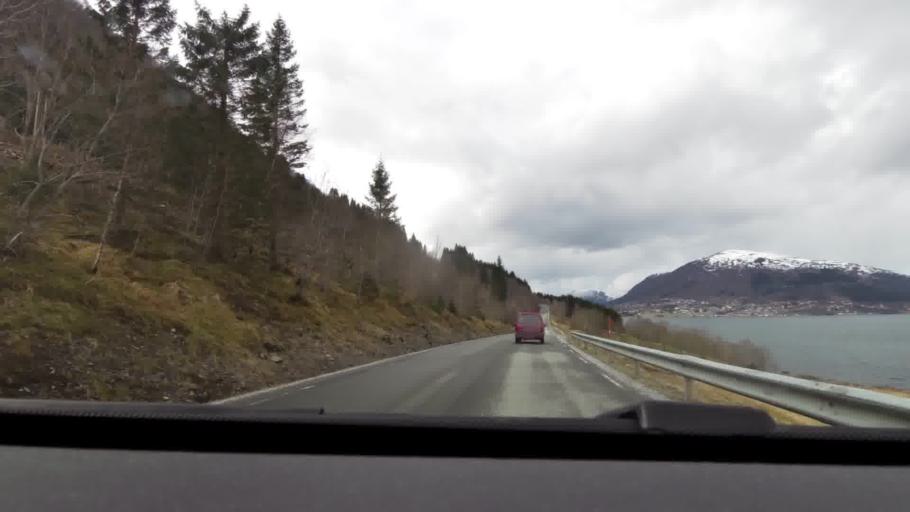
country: NO
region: More og Romsdal
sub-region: Eide
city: Eide
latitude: 62.9057
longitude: 7.5096
